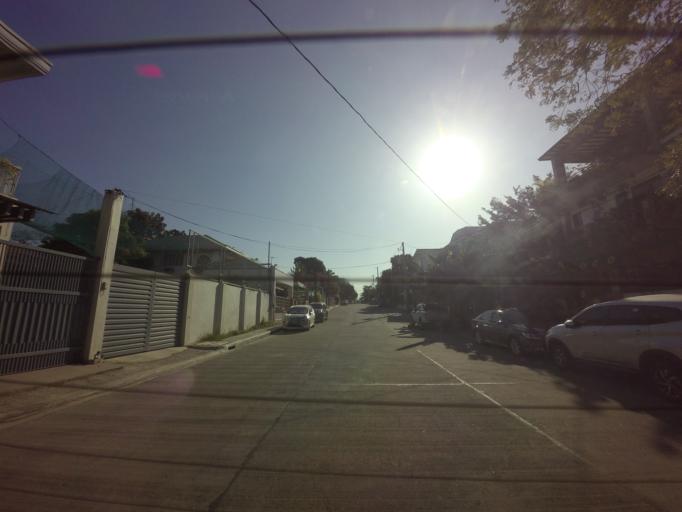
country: PH
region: Metro Manila
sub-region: Makati City
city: Makati City
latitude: 14.5304
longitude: 121.0389
